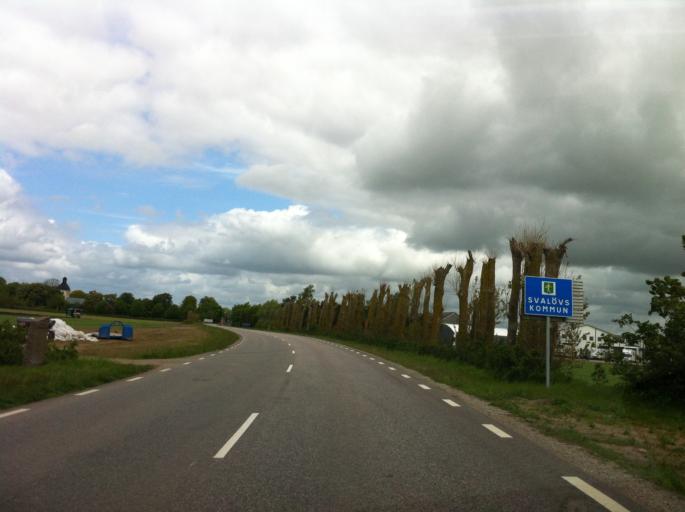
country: SE
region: Skane
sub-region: Svalovs Kommun
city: Teckomatorp
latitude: 55.8336
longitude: 13.0971
